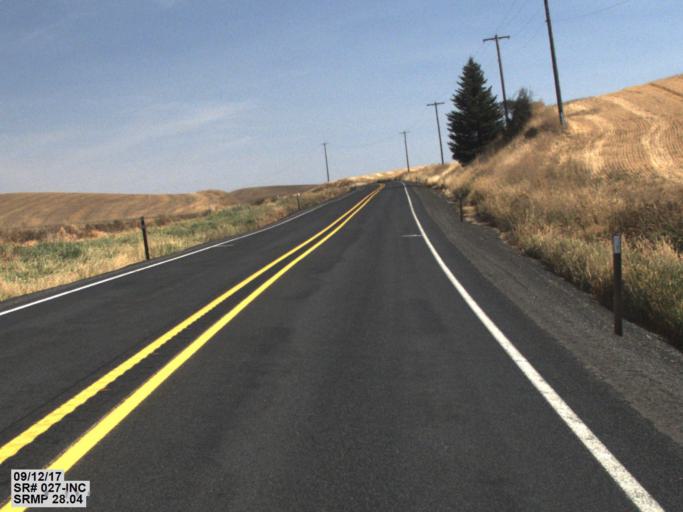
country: US
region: Washington
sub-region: Whitman County
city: Colfax
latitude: 47.0537
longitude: -117.1581
